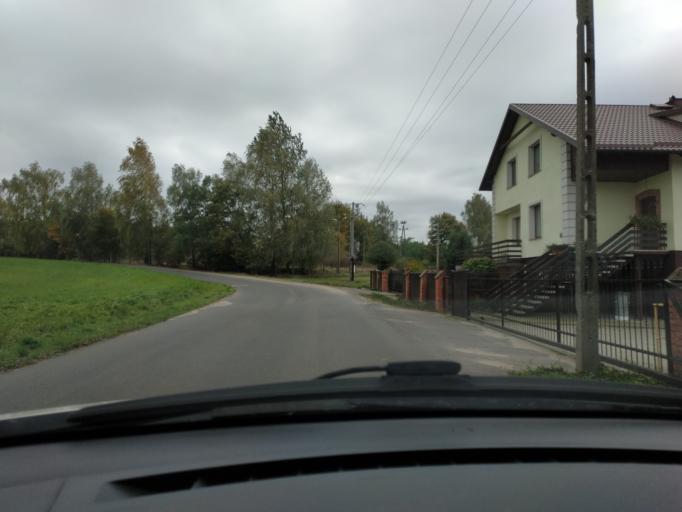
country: PL
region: Warmian-Masurian Voivodeship
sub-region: Powiat nowomiejski
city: Biskupiec
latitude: 53.4843
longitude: 19.3765
